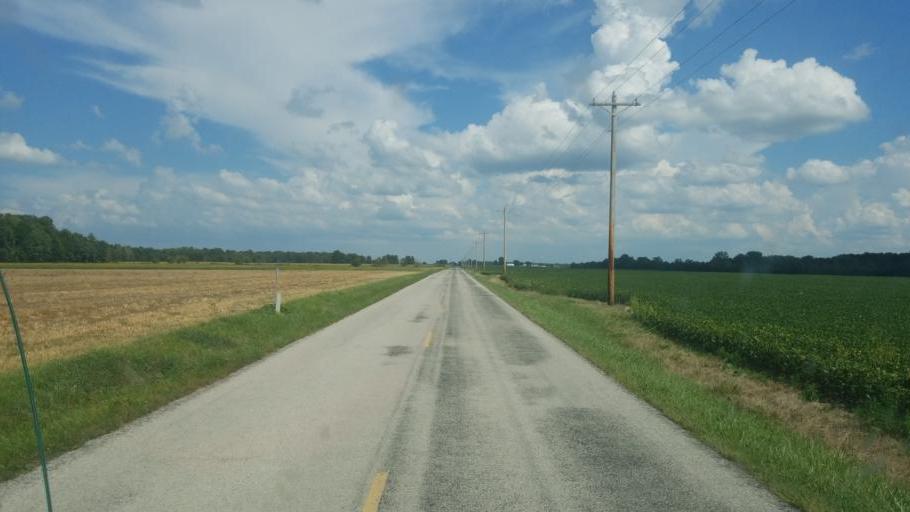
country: US
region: Ohio
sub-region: Seneca County
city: Tiffin
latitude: 40.9936
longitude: -83.0894
